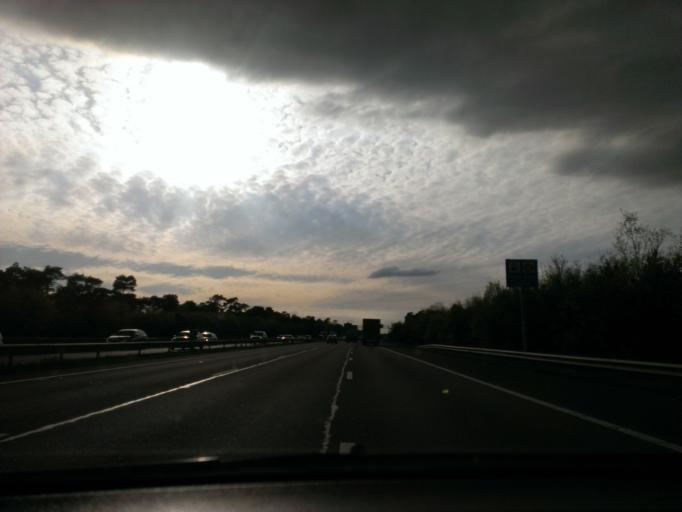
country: NL
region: Gelderland
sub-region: Gemeente Arnhem
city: Gulden Bodem
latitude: 52.0211
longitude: 5.8911
